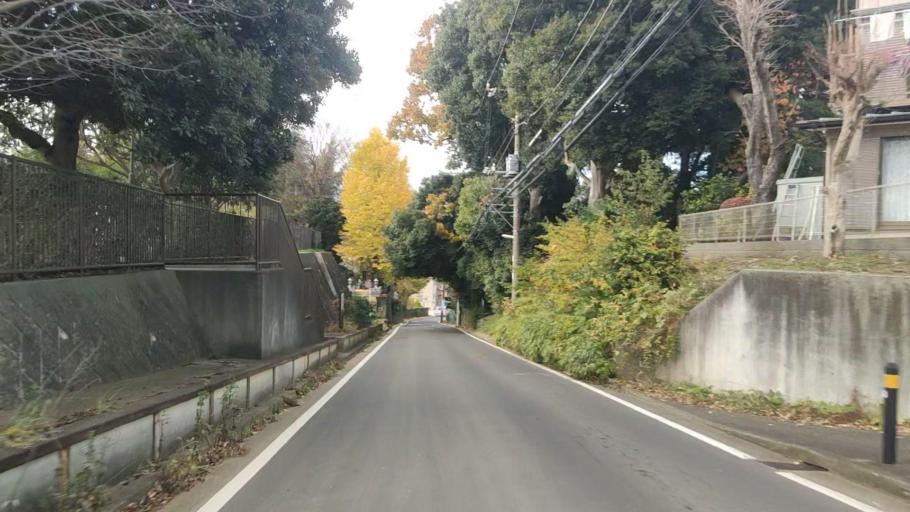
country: JP
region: Kanagawa
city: Minami-rinkan
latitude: 35.4901
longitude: 139.4762
